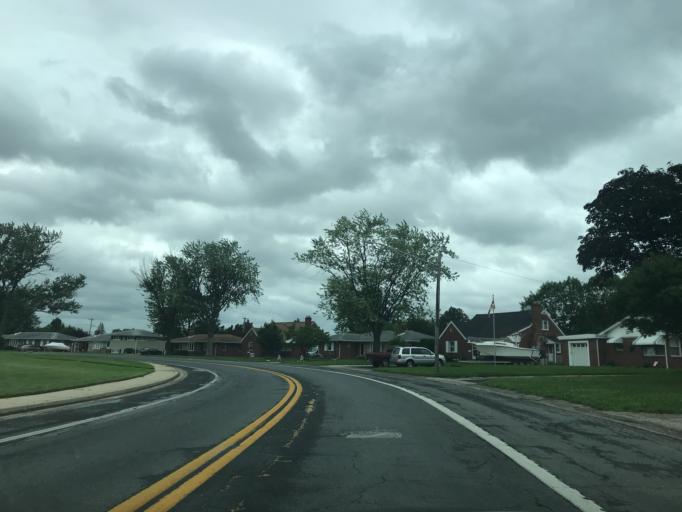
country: US
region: Maryland
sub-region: Anne Arundel County
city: Linthicum
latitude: 39.2046
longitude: -76.6429
